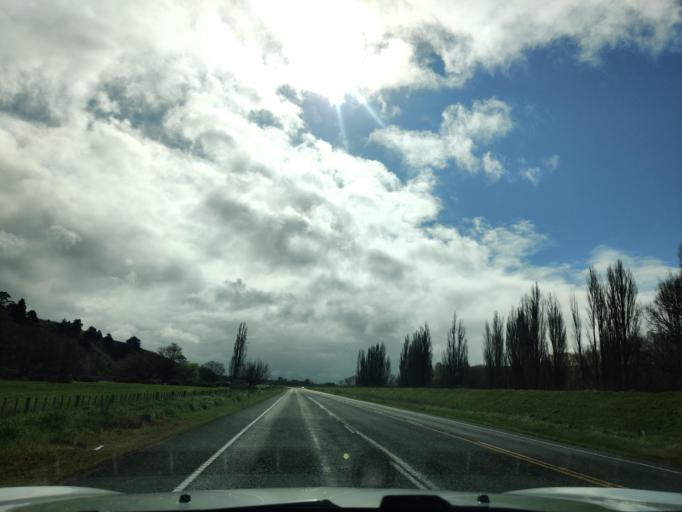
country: NZ
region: Hawke's Bay
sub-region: Hastings District
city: Hastings
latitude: -39.9839
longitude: 176.5082
